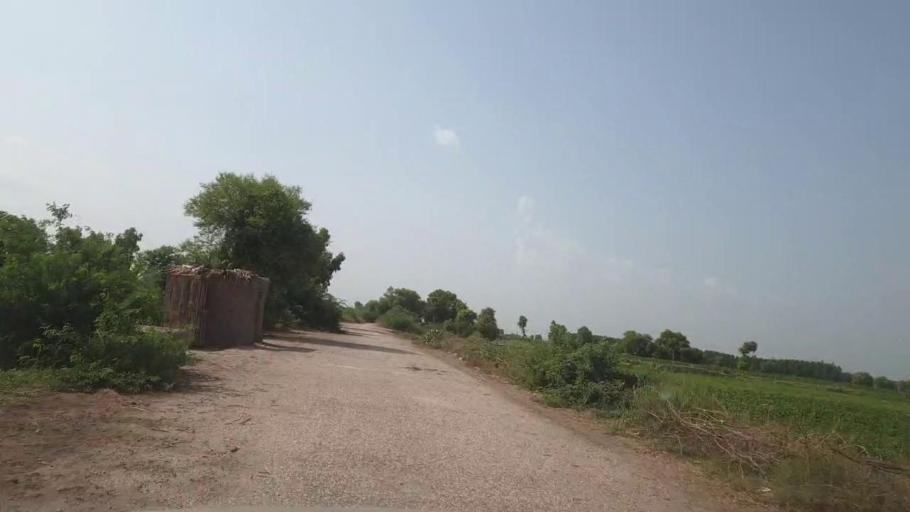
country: PK
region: Sindh
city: Pano Aqil
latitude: 27.7763
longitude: 69.1622
